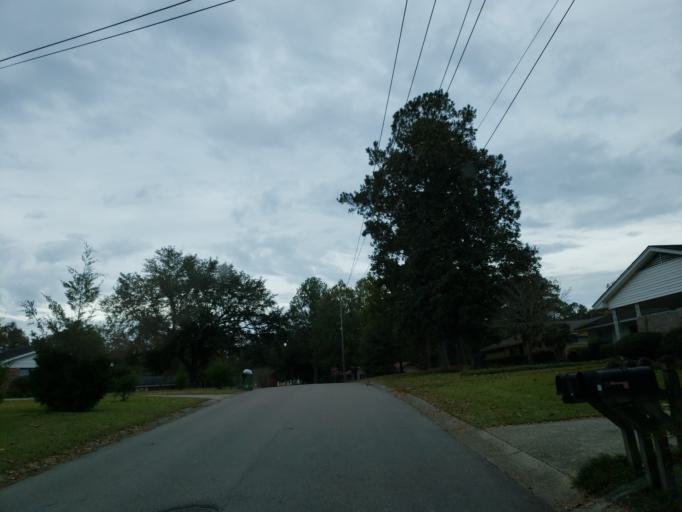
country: US
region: Mississippi
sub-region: Lamar County
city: West Hattiesburg
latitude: 31.3136
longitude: -89.3349
